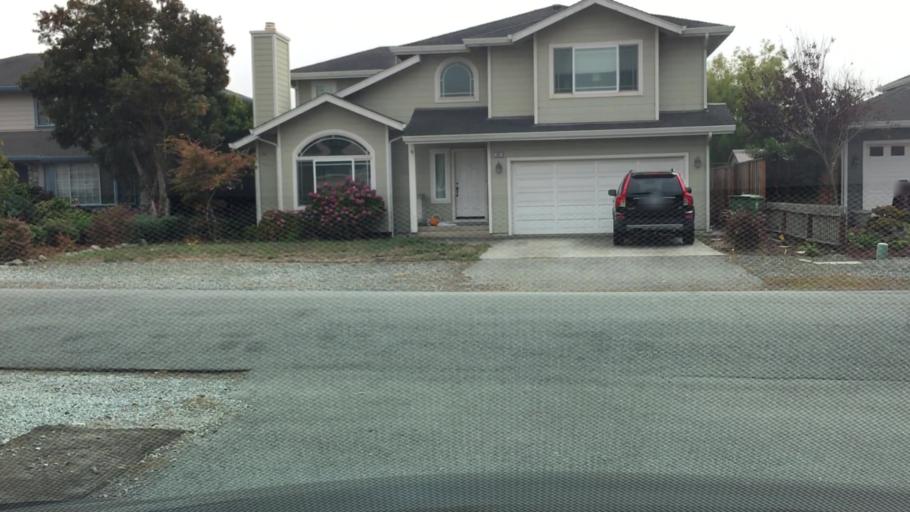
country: US
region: California
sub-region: San Mateo County
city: Half Moon Bay
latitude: 37.4562
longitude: -122.4378
